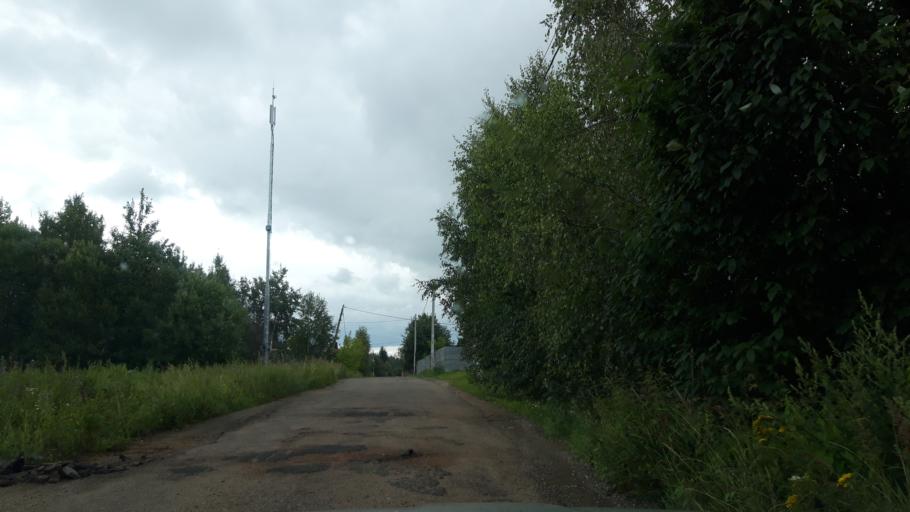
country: RU
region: Moskovskaya
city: Povarovo
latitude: 56.0953
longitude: 37.0712
